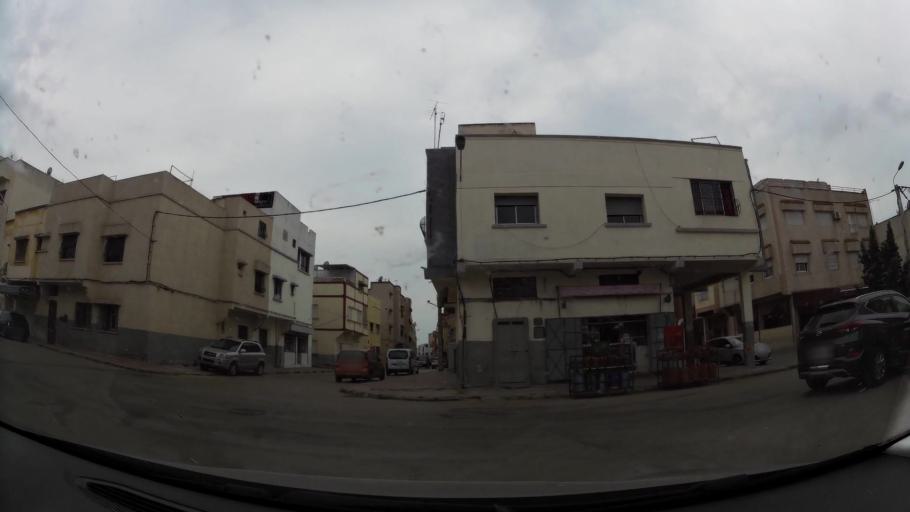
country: MA
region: Rabat-Sale-Zemmour-Zaer
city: Sale
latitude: 34.0279
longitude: -6.8030
